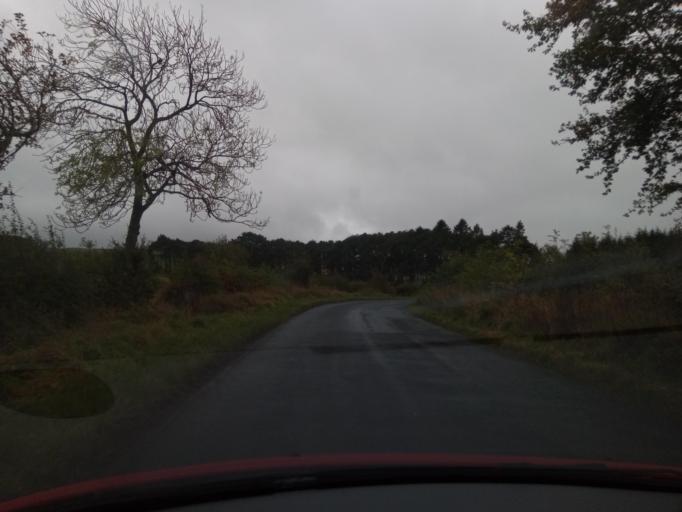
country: GB
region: Scotland
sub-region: The Scottish Borders
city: Melrose
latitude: 55.5120
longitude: -2.7499
